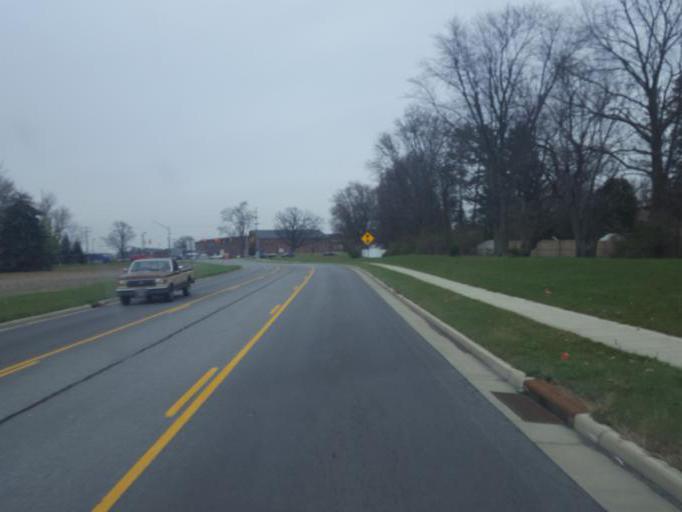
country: US
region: Ohio
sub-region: Marion County
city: Marion
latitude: 40.5891
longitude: -83.0903
